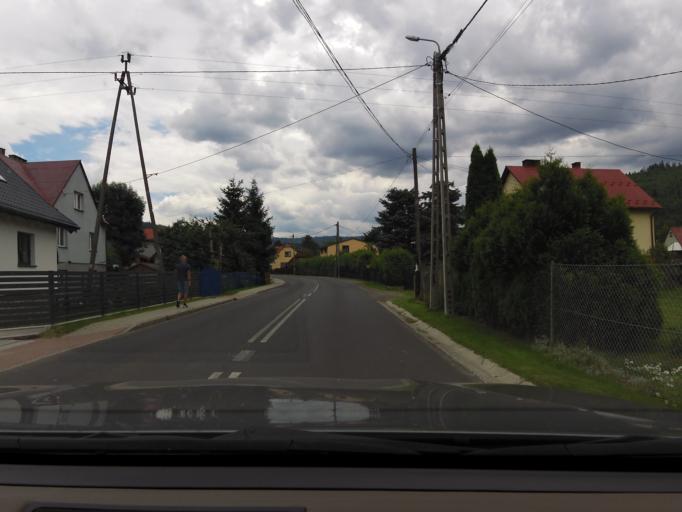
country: PL
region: Silesian Voivodeship
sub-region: Powiat zywiecki
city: Ujsoly
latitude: 49.4842
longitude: 19.1354
